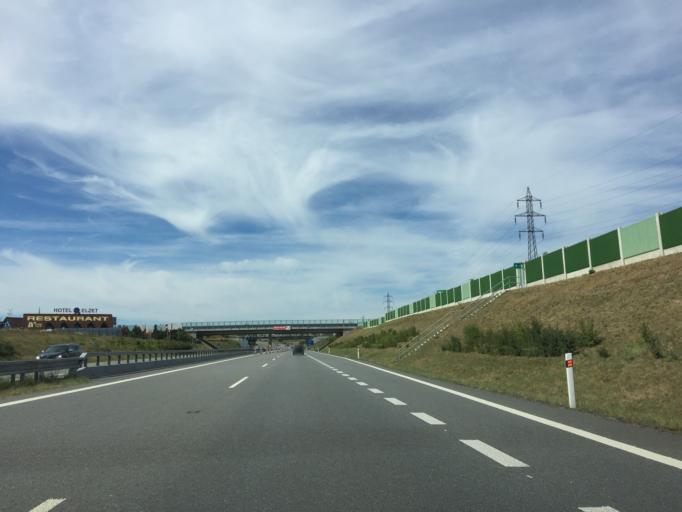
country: CZ
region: Jihocesky
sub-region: Okres Tabor
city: Sezimovo Usti
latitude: 49.4032
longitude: 14.7198
